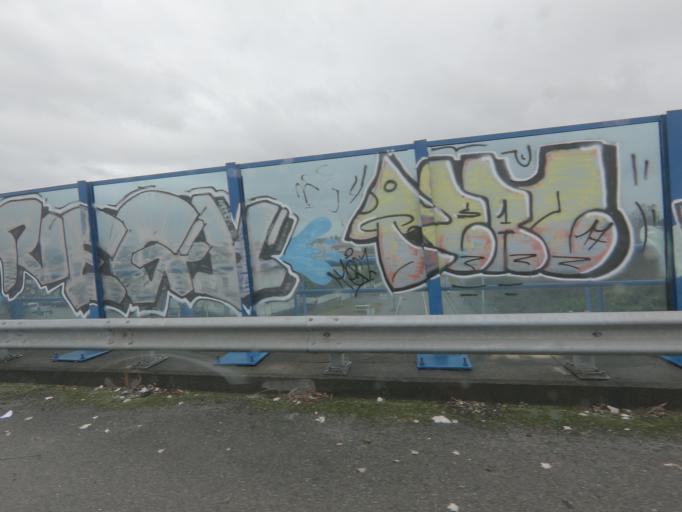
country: PT
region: Porto
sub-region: Matosinhos
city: Senhora da Hora
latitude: 41.2053
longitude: -8.6383
